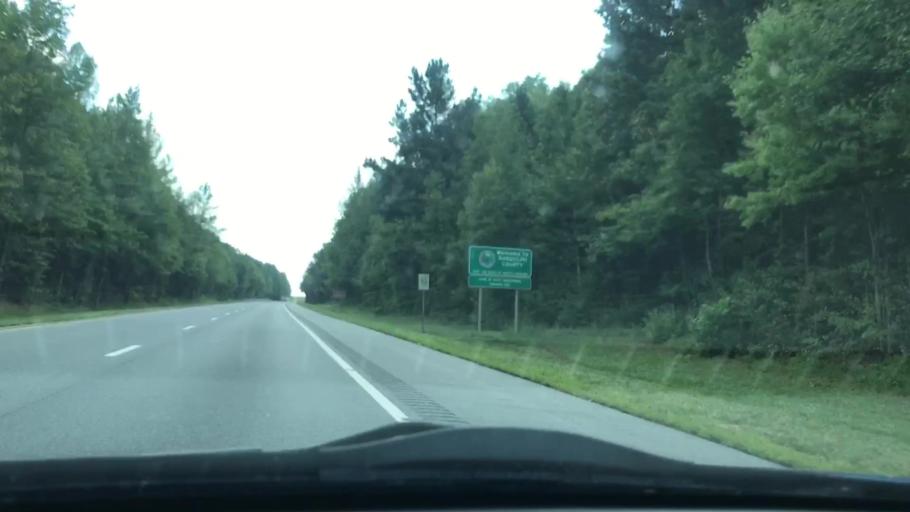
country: US
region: North Carolina
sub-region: Guilford County
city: Pleasant Garden
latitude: 35.9116
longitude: -79.8231
